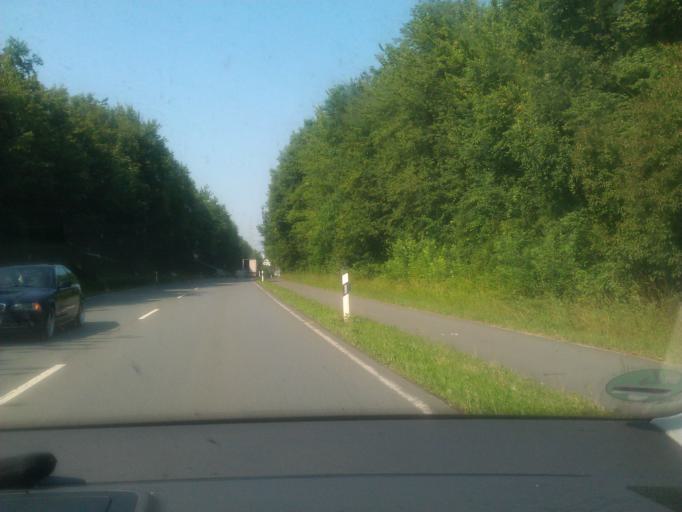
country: DE
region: North Rhine-Westphalia
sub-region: Regierungsbezirk Detmold
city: Leopoldshohe
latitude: 52.0039
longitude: 8.6964
